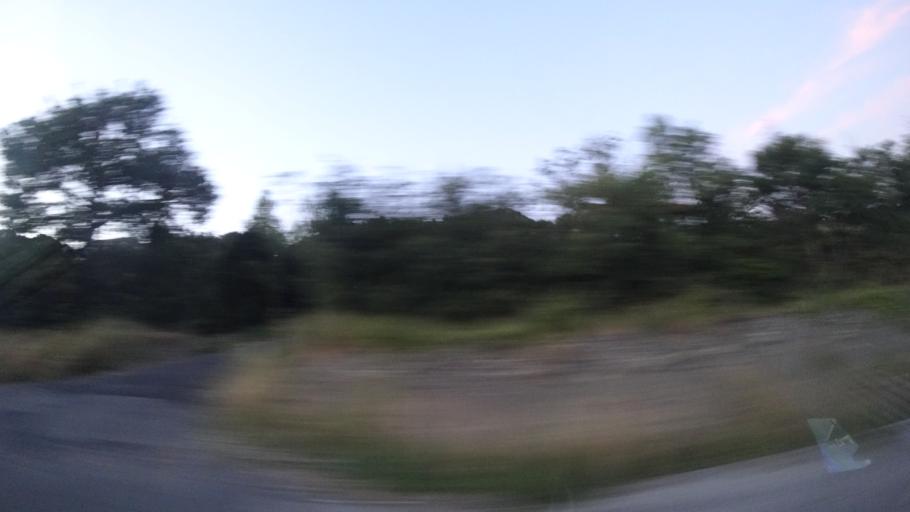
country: FR
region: Midi-Pyrenees
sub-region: Departement de l'Aveyron
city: Millau
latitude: 44.1284
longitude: 3.0525
